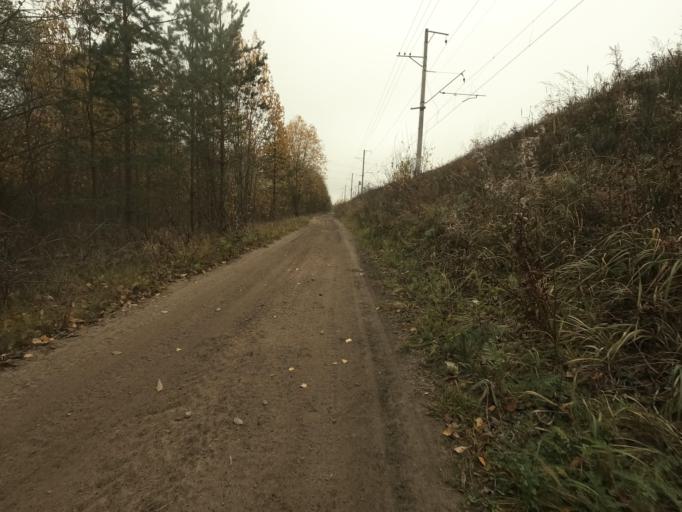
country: RU
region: Leningrad
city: Pavlovo
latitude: 59.7779
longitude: 30.8995
